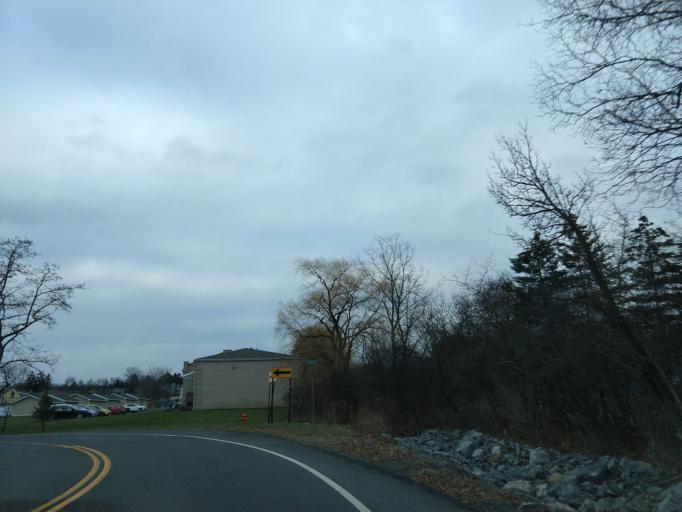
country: US
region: New York
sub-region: Tompkins County
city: Lansing
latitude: 42.4783
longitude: -76.4787
